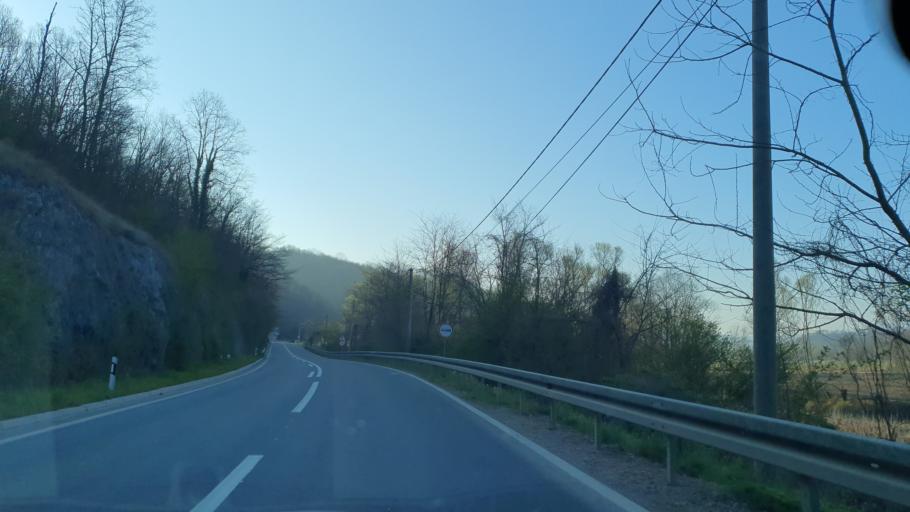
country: RS
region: Central Serbia
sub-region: Kolubarski Okrug
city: Osecina
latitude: 44.4063
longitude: 19.5545
